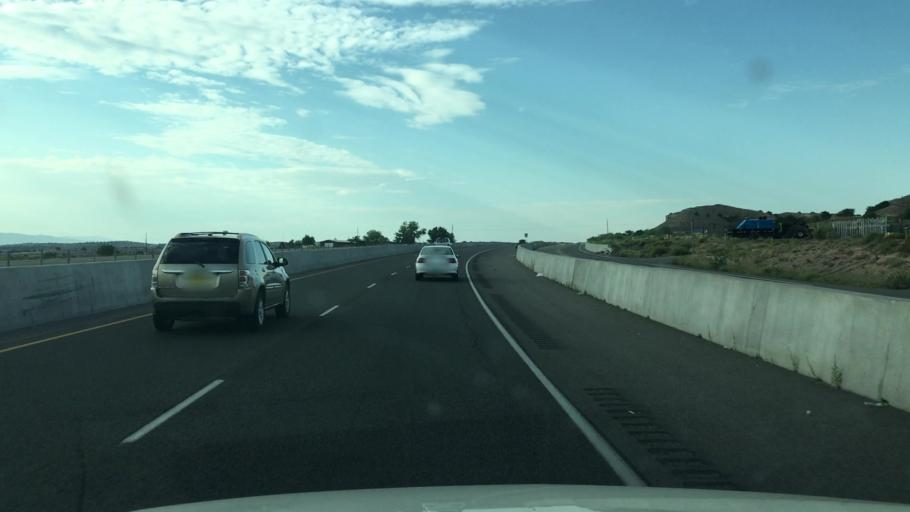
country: US
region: New Mexico
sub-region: Santa Fe County
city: El Valle de Arroyo Seco
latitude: 35.9536
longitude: -106.0214
